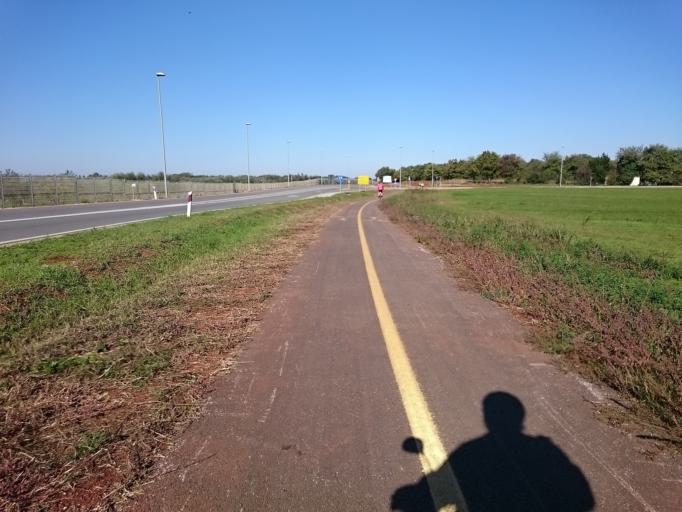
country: HR
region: Istarska
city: Umag
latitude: 45.4123
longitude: 13.5296
